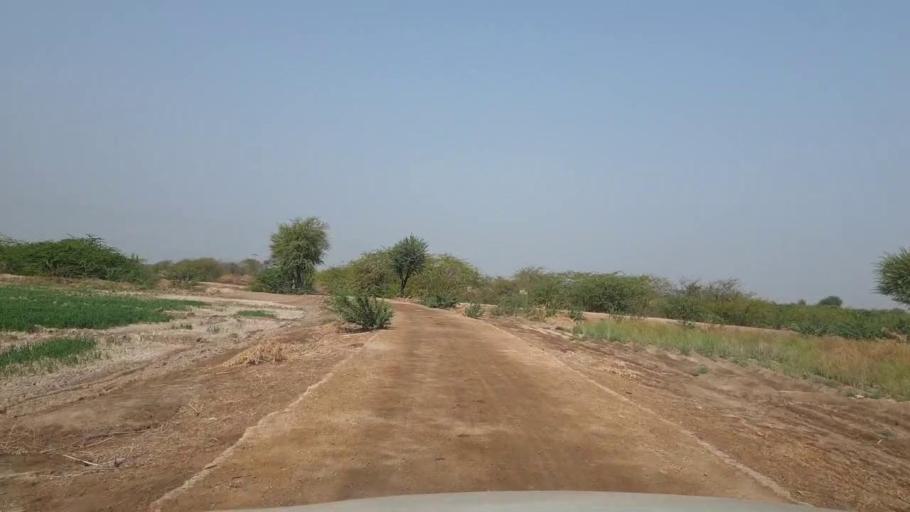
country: PK
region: Sindh
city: Chor
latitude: 25.4744
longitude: 69.7089
